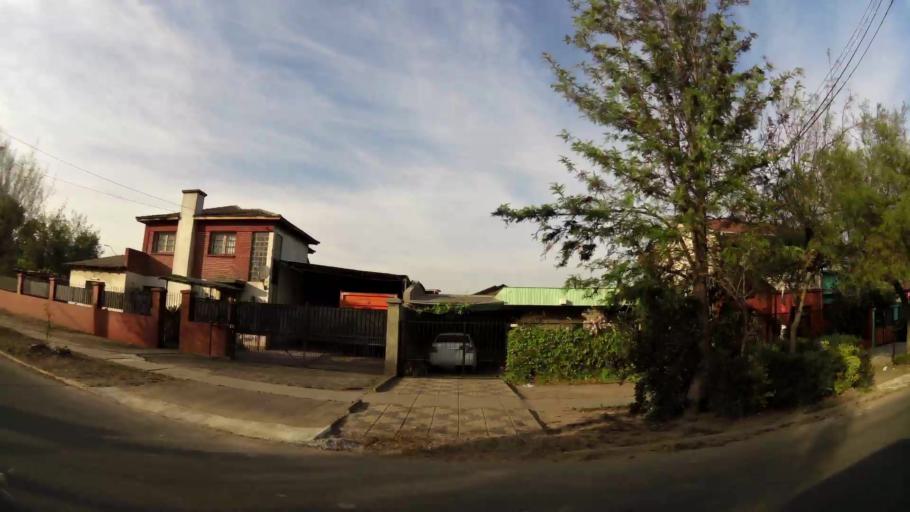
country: CL
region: Santiago Metropolitan
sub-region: Provincia de Santiago
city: La Pintana
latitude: -33.5323
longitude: -70.6732
